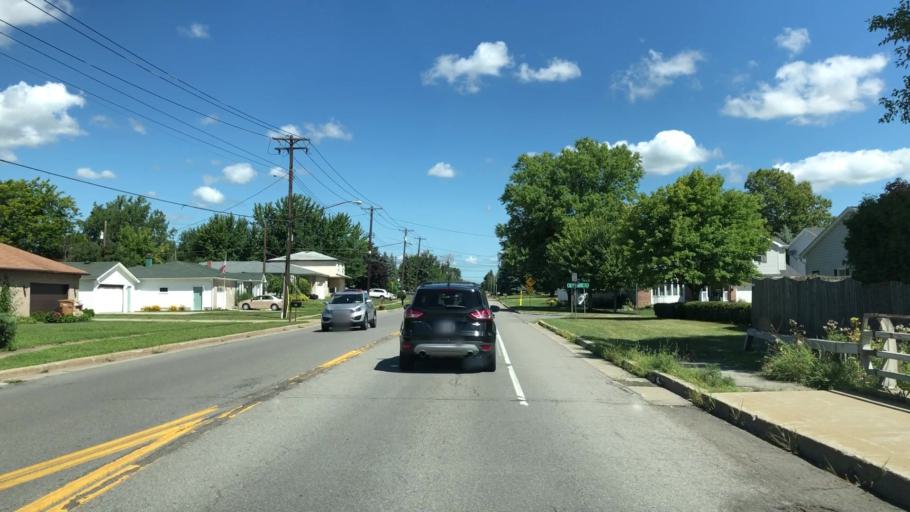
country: US
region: New York
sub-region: Erie County
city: Depew
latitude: 42.8685
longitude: -78.7090
